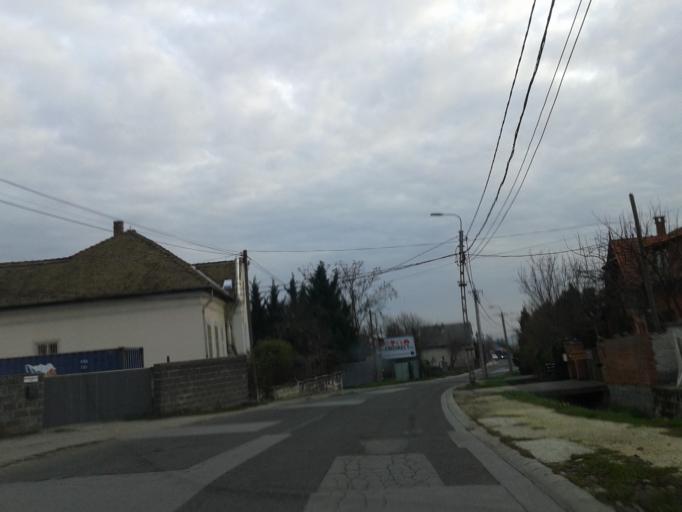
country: HU
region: Pest
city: Diosd
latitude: 47.4096
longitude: 18.9907
